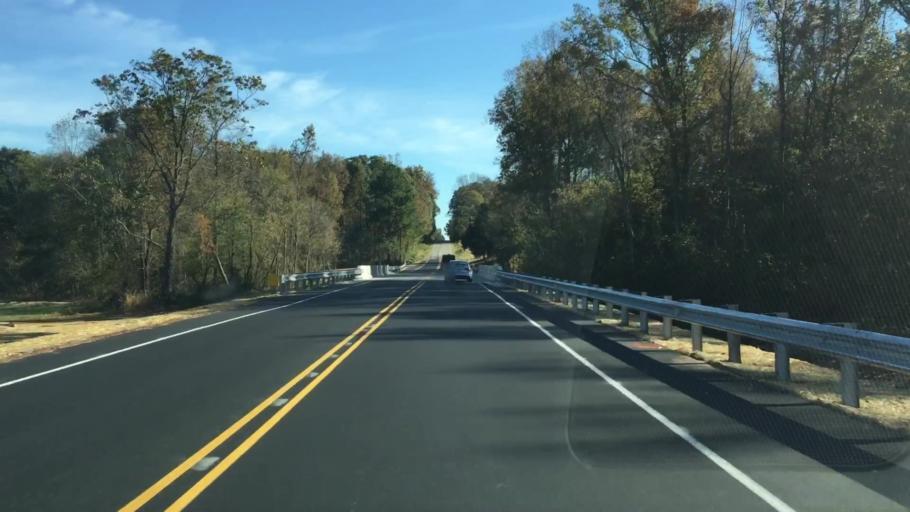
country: US
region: North Carolina
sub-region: Rowan County
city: China Grove
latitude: 35.6425
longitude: -80.6504
